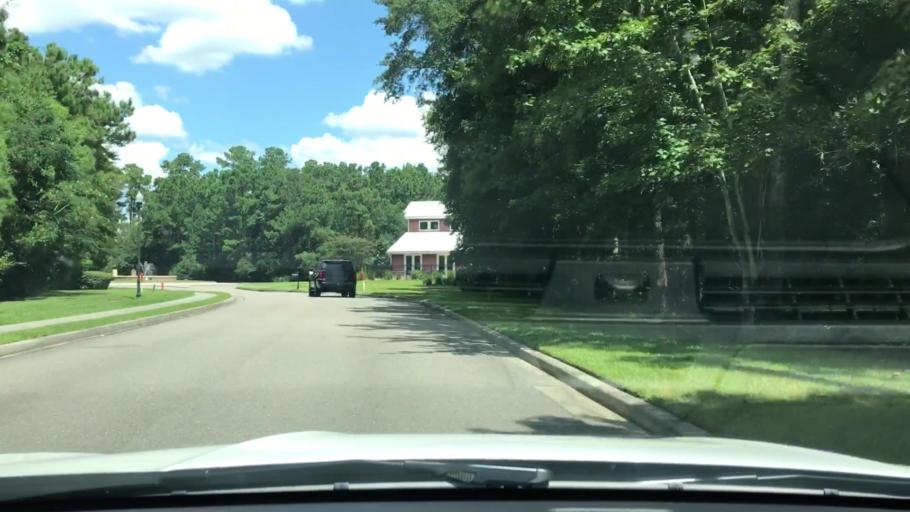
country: US
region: South Carolina
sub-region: Berkeley County
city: Hanahan
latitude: 32.9301
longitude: -79.9997
